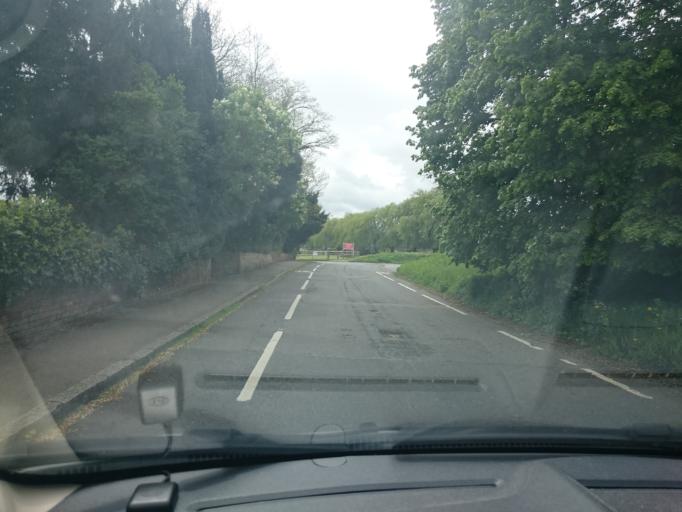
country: GB
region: England
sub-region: Surrey
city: Pirbright
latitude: 51.2655
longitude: -0.6186
